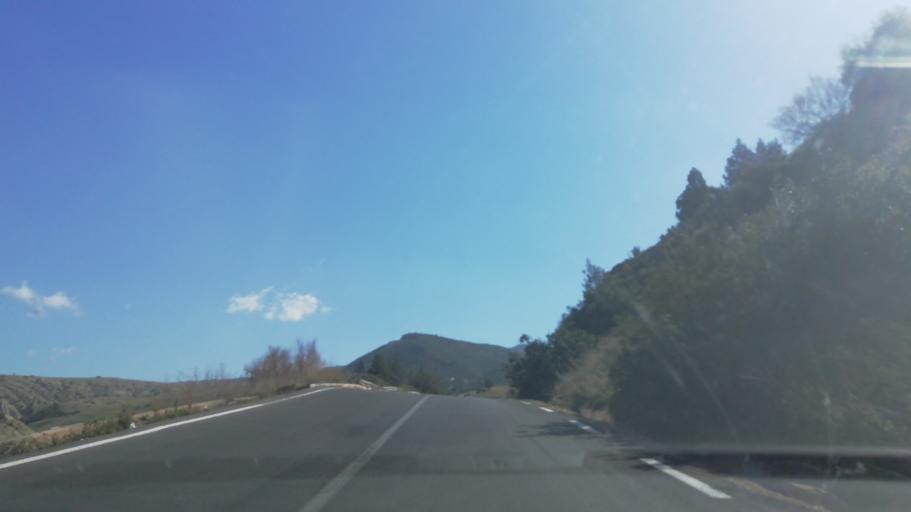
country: DZ
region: Mascara
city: Mascara
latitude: 35.4995
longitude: 0.1329
